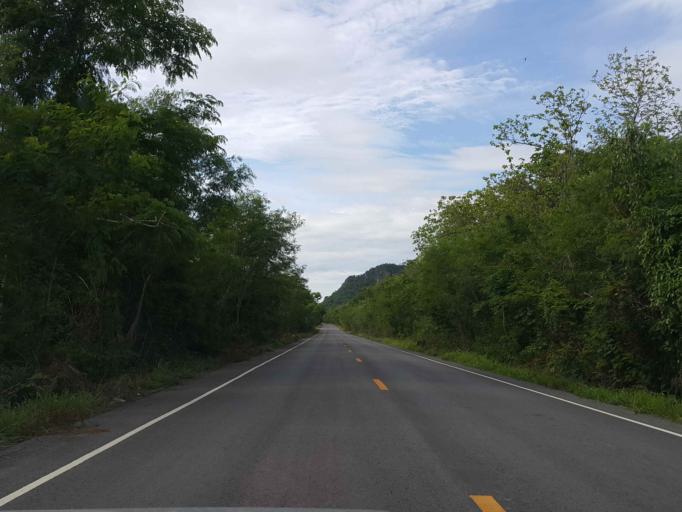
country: TH
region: Sukhothai
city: Thung Saliam
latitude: 17.2934
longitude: 99.5269
